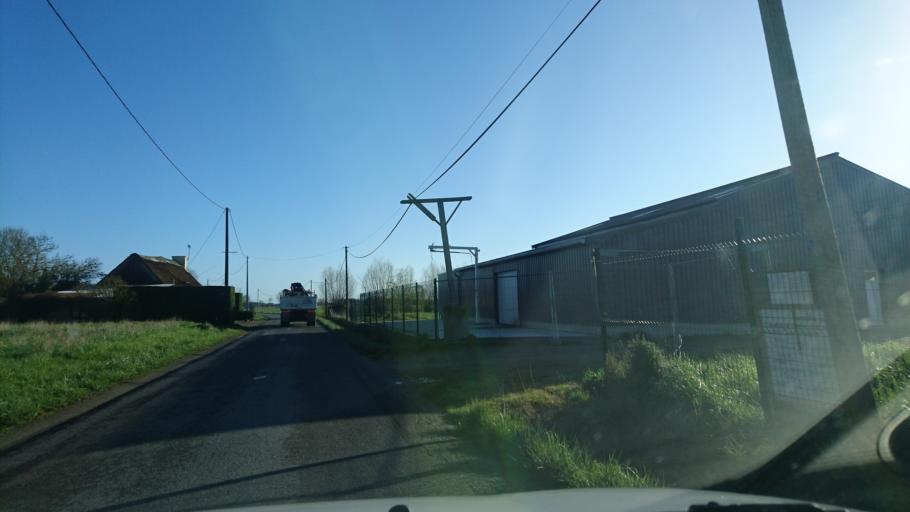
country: FR
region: Brittany
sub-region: Departement d'Ille-et-Vilaine
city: Cherrueix
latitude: 48.5911
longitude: -1.7192
